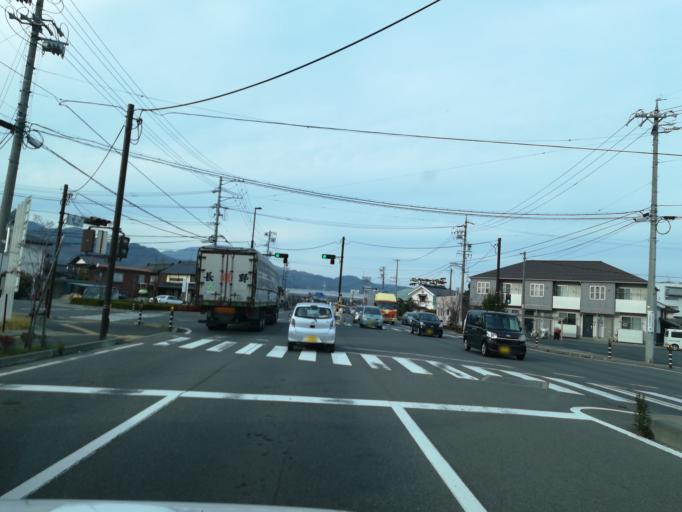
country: JP
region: Nagano
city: Nagano-shi
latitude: 36.6051
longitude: 138.1788
